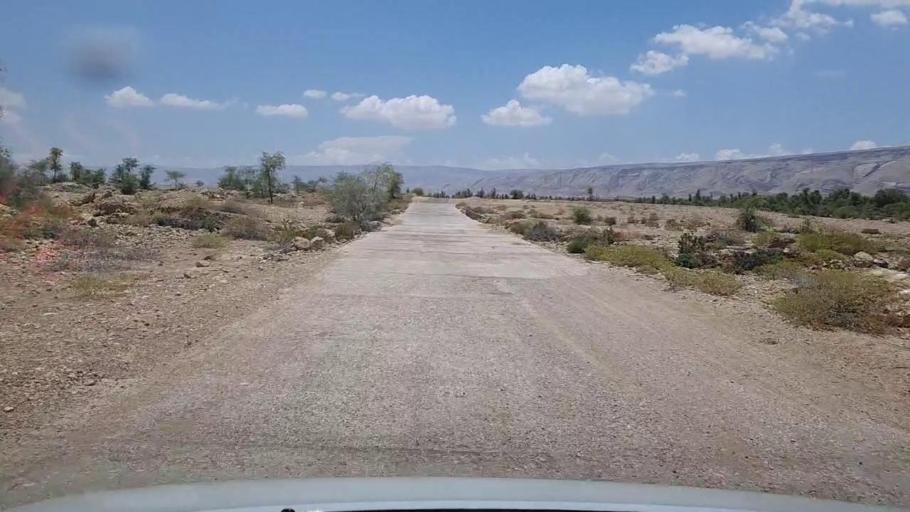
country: PK
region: Sindh
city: Bhan
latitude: 26.2851
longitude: 67.5325
